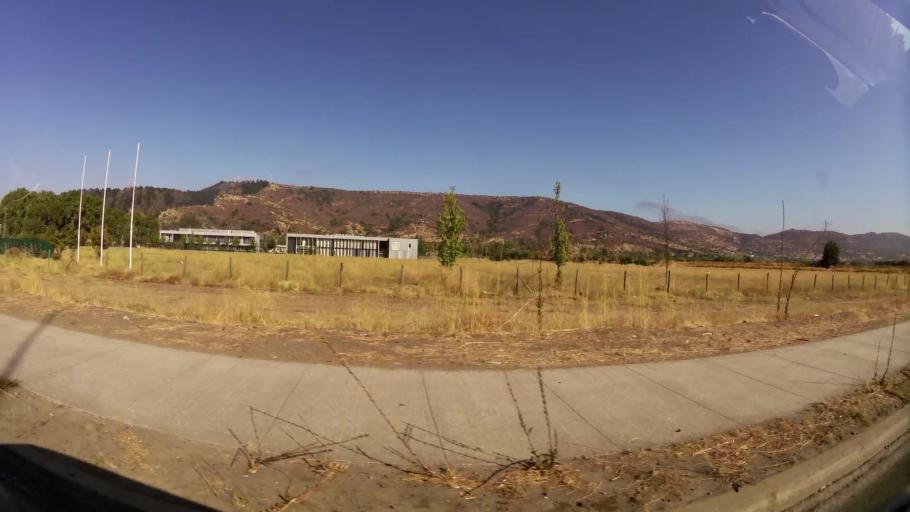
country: CL
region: Maule
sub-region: Provincia de Talca
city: Talca
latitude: -35.4159
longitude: -71.6735
